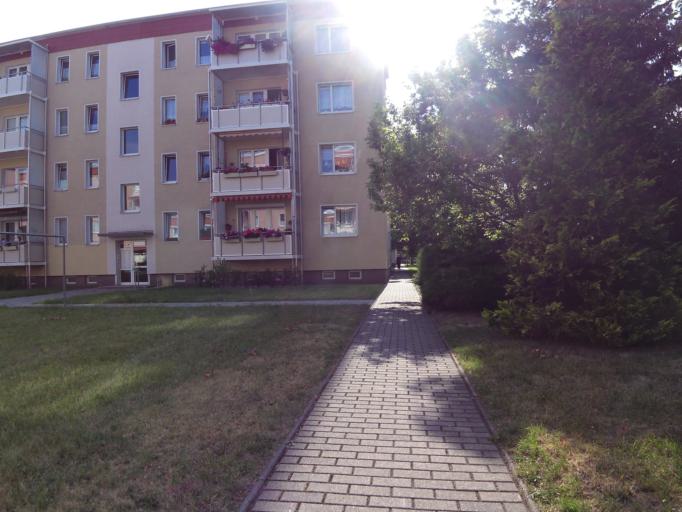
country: DE
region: Saxony
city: Leipzig
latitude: 51.3581
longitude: 12.4237
